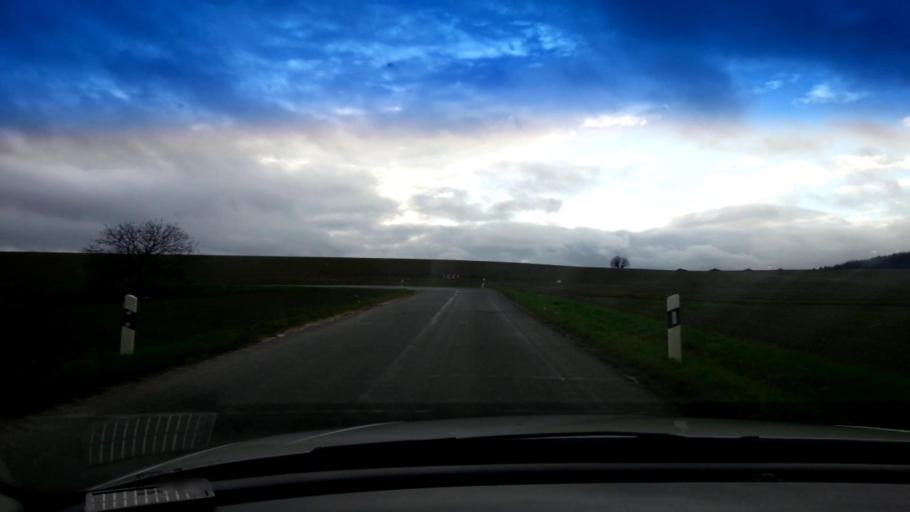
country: DE
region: Bavaria
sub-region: Upper Franconia
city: Zapfendorf
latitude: 50.0287
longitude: 10.9688
